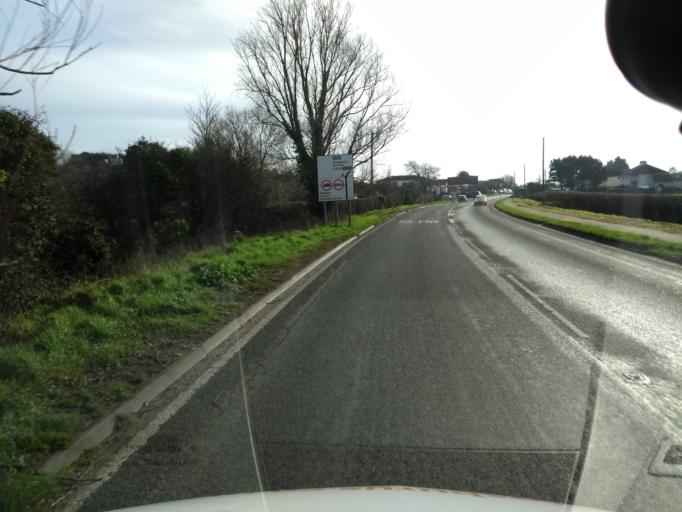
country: GB
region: England
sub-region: North Somerset
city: Bleadon
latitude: 51.3048
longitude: -2.9501
